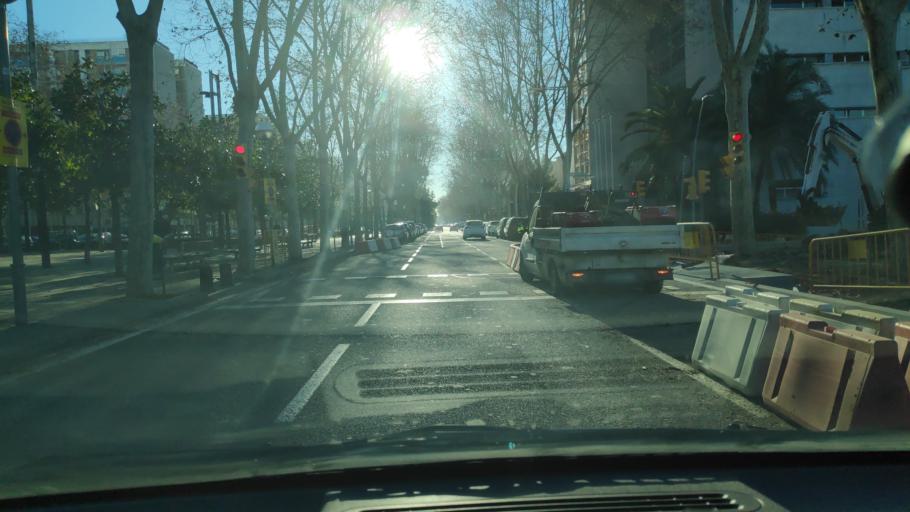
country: ES
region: Catalonia
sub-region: Provincia de Barcelona
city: Sant Marti
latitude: 41.4170
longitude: 2.2115
